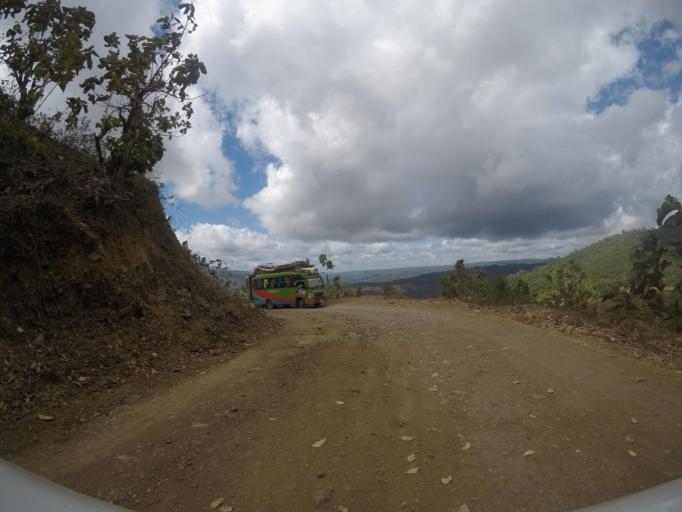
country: TL
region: Lautem
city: Lospalos
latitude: -8.5417
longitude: 126.8373
